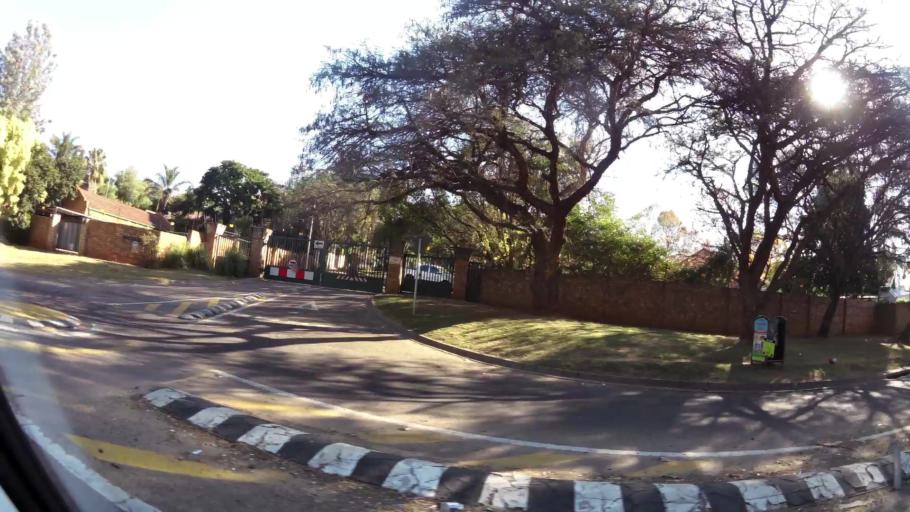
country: ZA
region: Gauteng
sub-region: City of Tshwane Metropolitan Municipality
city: Centurion
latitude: -25.8200
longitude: 28.2949
